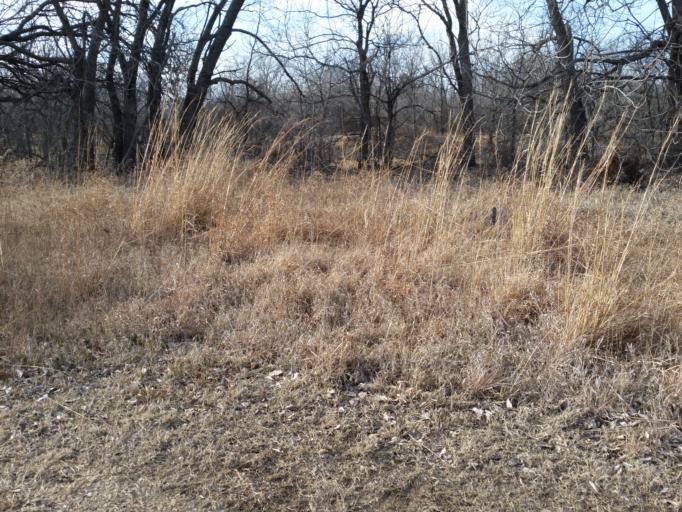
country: US
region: Kansas
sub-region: Harvey County
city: North Newton
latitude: 38.0624
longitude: -97.3399
